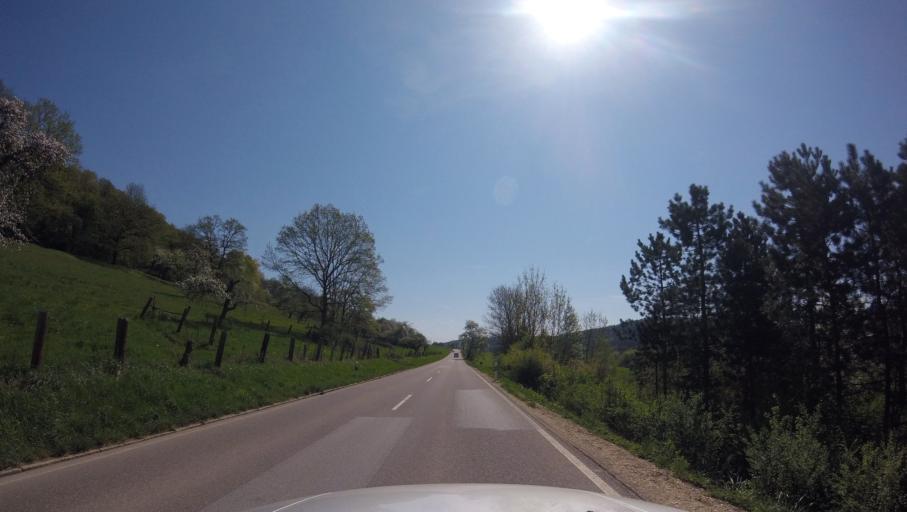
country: DE
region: Baden-Wuerttemberg
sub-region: Regierungsbezirk Stuttgart
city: Lorch
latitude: 48.7951
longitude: 9.7207
